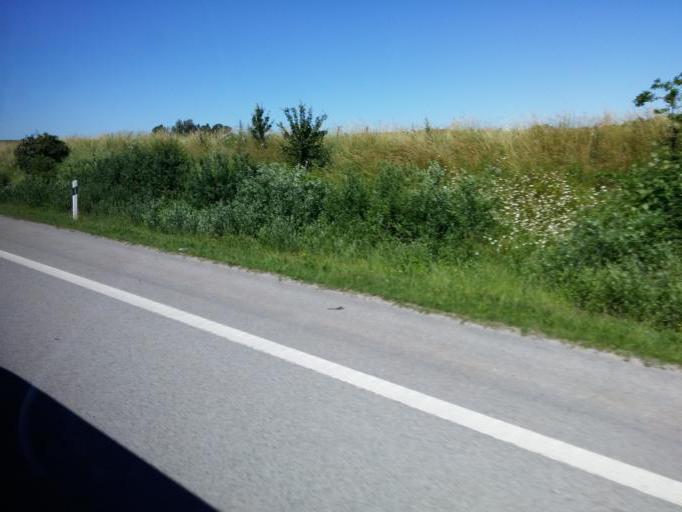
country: SE
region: Skane
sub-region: Malmo
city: Oxie
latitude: 55.5555
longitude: 13.0997
